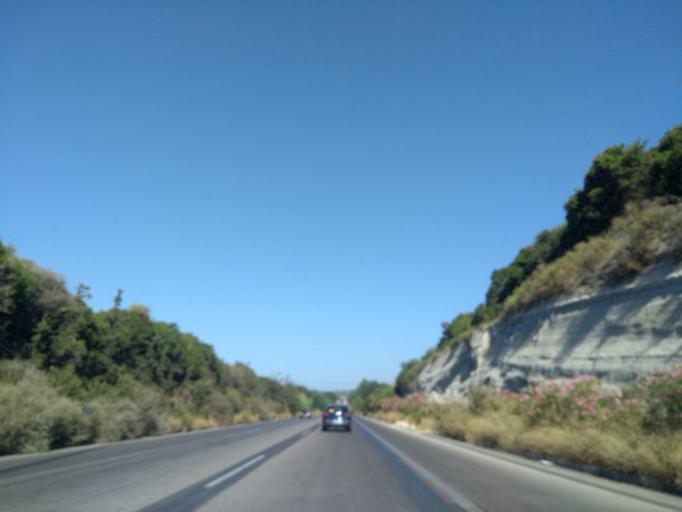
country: GR
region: Crete
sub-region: Nomos Chanias
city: Gerani
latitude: 35.5147
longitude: 23.8719
